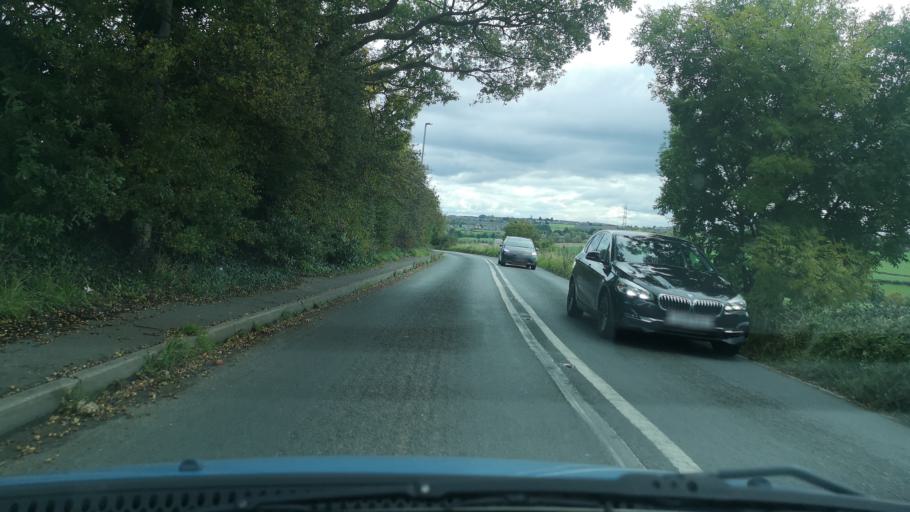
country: GB
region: England
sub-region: City and Borough of Wakefield
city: Middlestown
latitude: 53.6621
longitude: -1.6038
